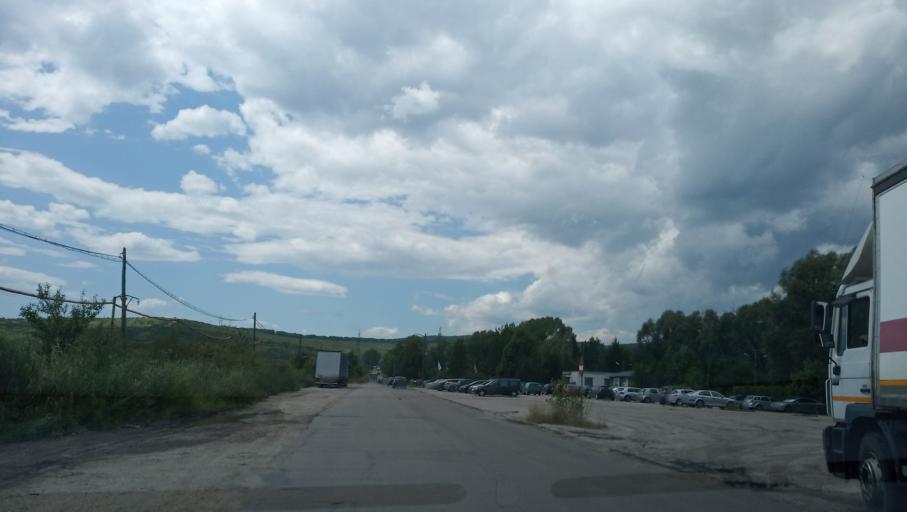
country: RO
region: Valcea
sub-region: Municipiul Ramnicu Valcea
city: Stolniceni
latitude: 45.0456
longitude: 24.2865
